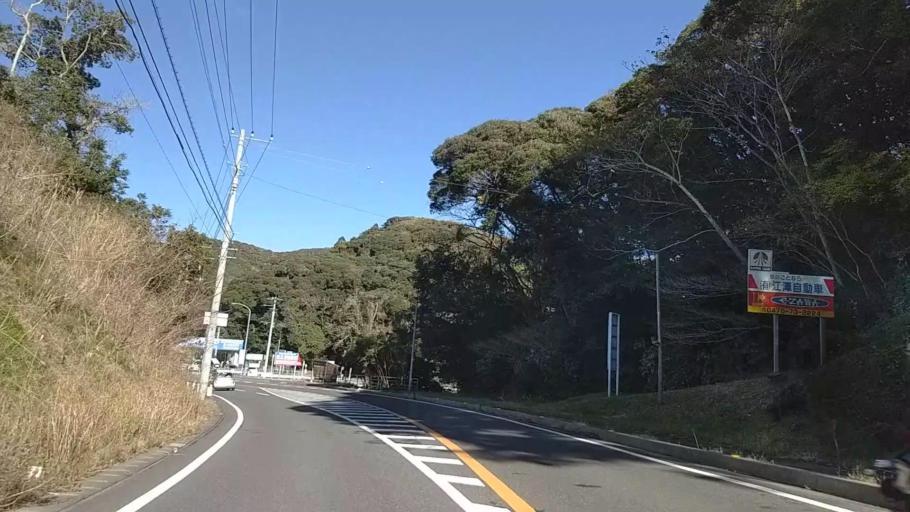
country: JP
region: Chiba
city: Katsuura
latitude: 35.1585
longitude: 140.3268
